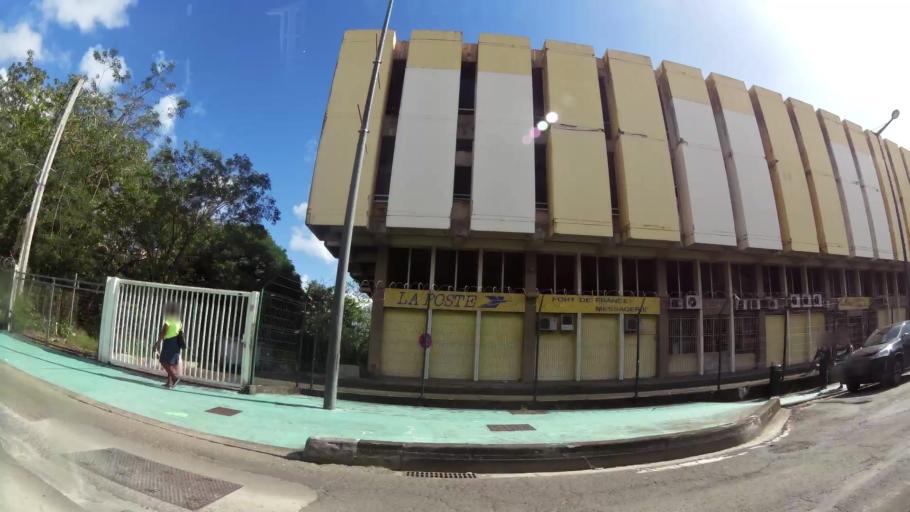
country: MQ
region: Martinique
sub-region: Martinique
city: Fort-de-France
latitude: 14.6044
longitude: -61.0651
